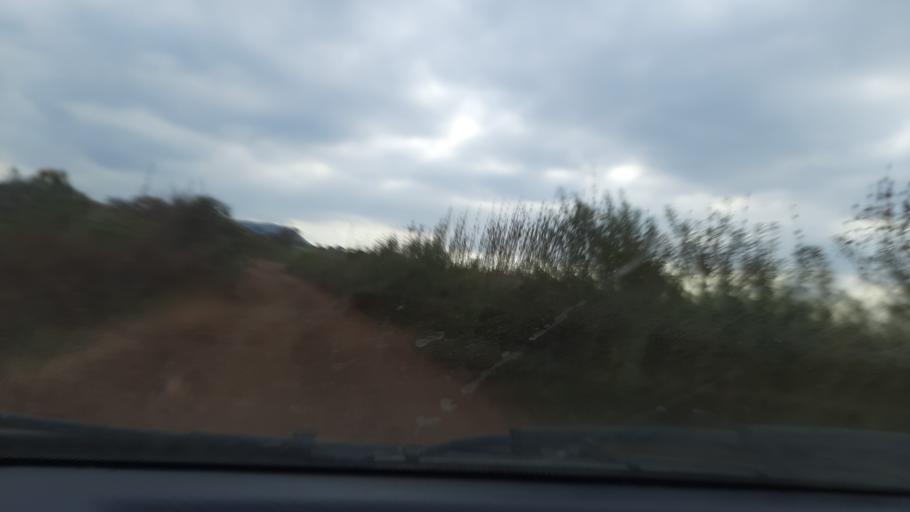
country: TZ
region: Arusha
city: Kingori
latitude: -2.8445
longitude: 37.2228
